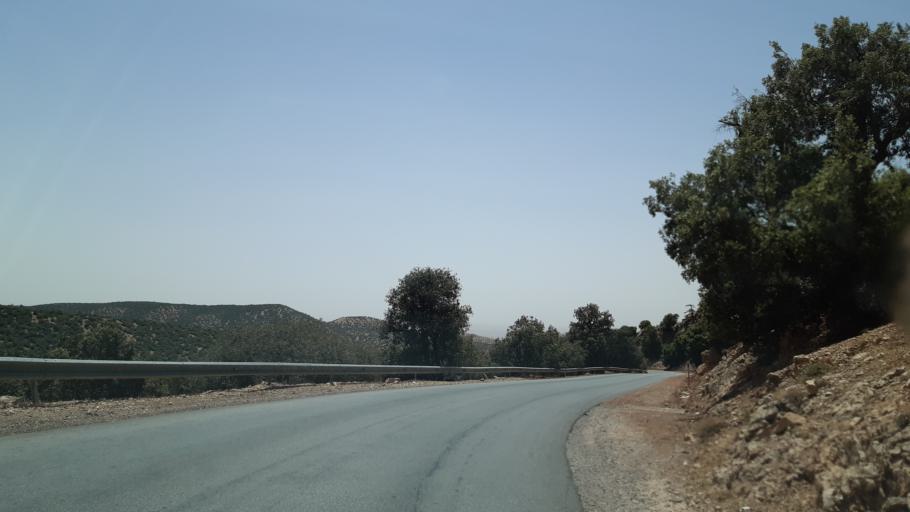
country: MA
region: Meknes-Tafilalet
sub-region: Khenifra
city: Itzer
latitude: 32.9741
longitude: -5.0587
